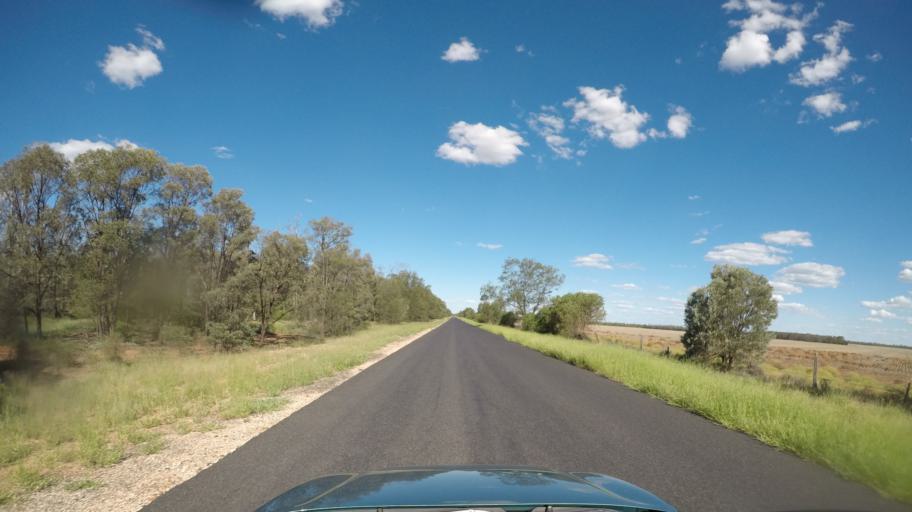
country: AU
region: Queensland
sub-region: Goondiwindi
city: Goondiwindi
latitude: -28.1644
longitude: 150.4307
